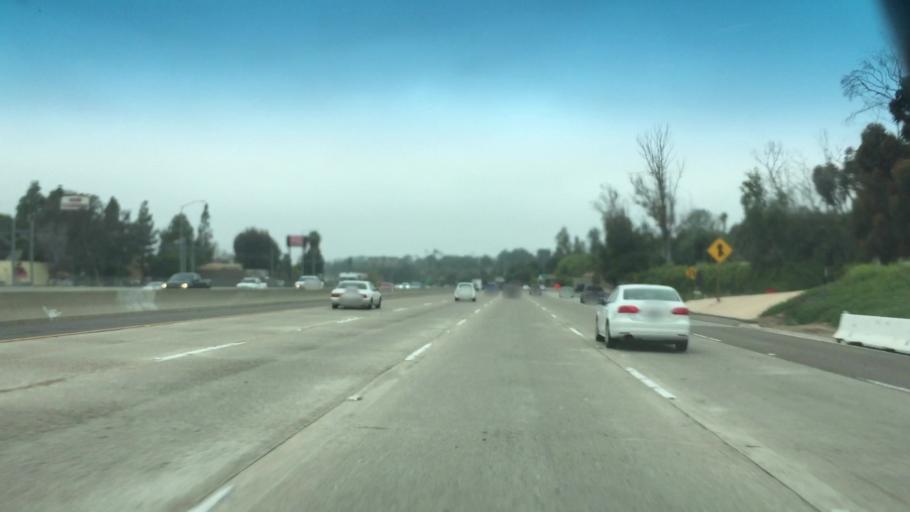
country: US
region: California
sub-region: San Diego County
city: La Mesa
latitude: 32.7746
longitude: -117.0465
